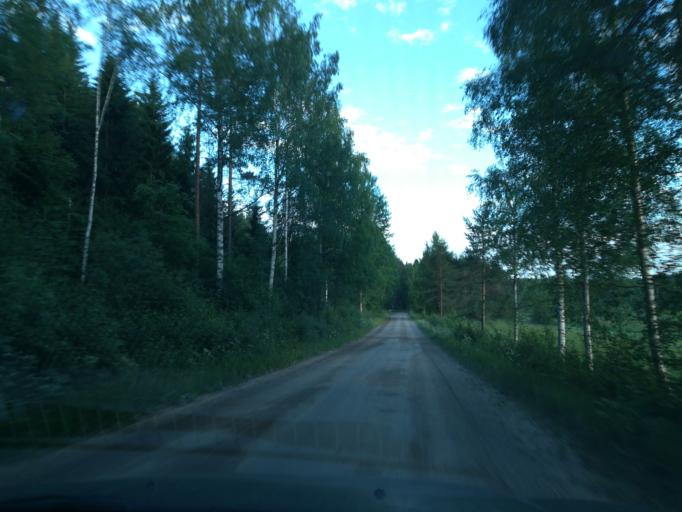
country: FI
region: Southern Savonia
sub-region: Mikkeli
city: Puumala
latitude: 61.6083
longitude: 28.1155
